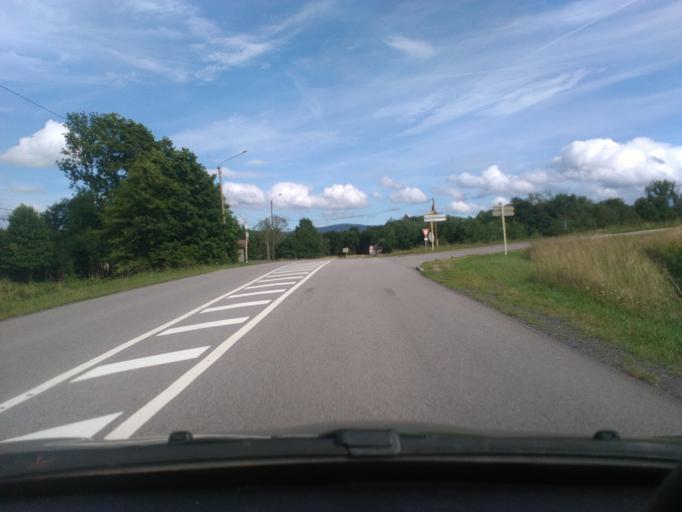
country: FR
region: Lorraine
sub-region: Departement des Vosges
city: Corcieux
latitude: 48.1993
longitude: 6.8537
